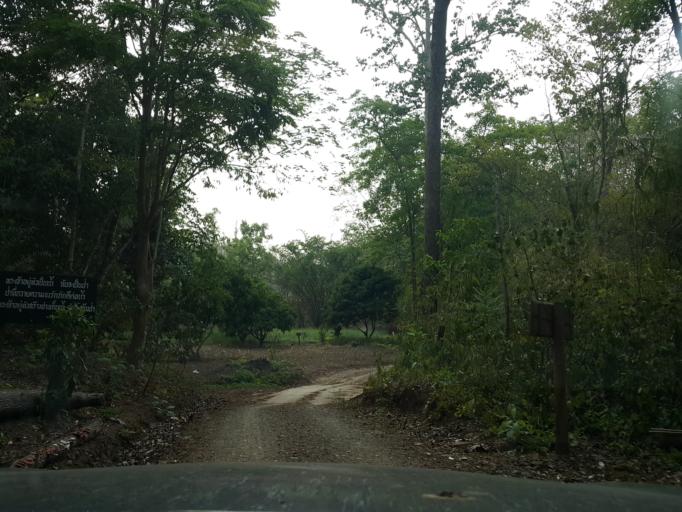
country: TH
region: Lamphun
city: Li
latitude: 17.6127
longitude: 98.9584
